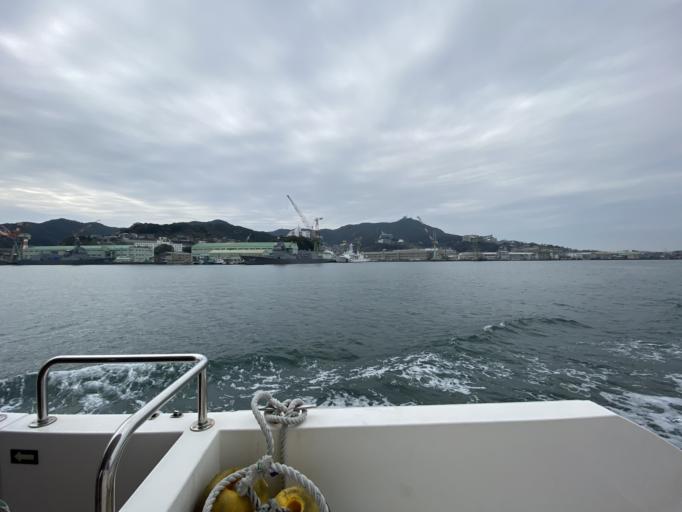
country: JP
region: Nagasaki
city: Nagasaki-shi
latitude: 32.7358
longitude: 129.8618
